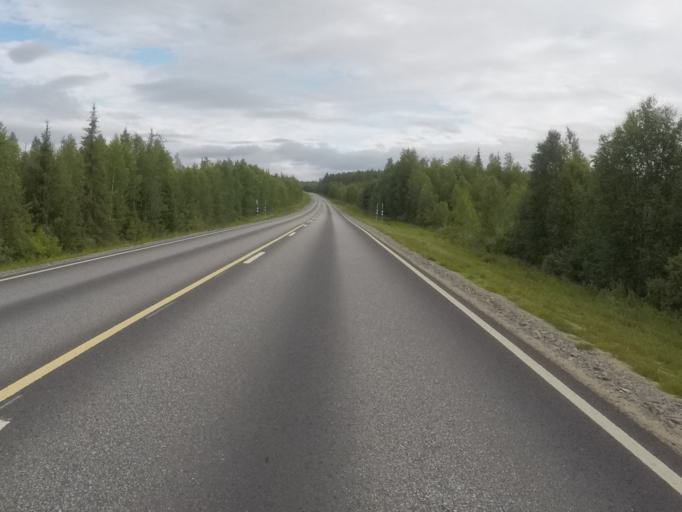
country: FI
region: Lapland
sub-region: Tunturi-Lappi
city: Kolari
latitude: 67.3917
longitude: 23.8067
